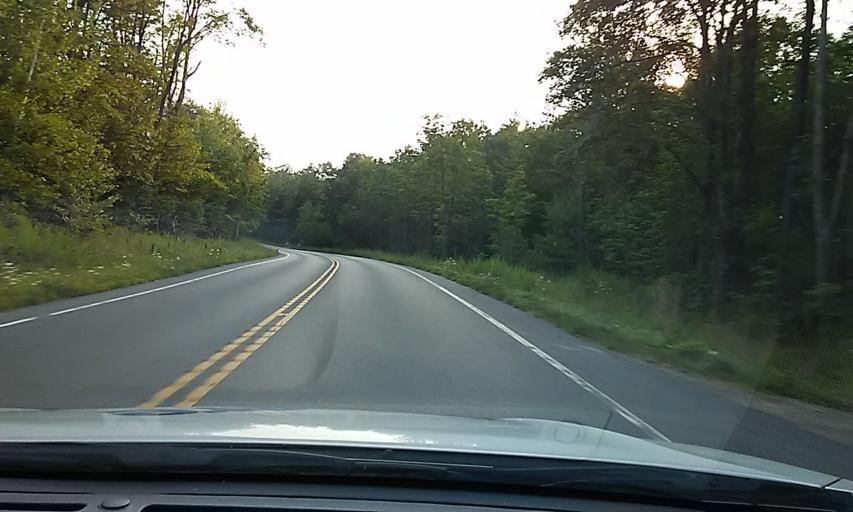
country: US
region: Pennsylvania
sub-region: McKean County
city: Kane
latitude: 41.5823
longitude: -78.8631
